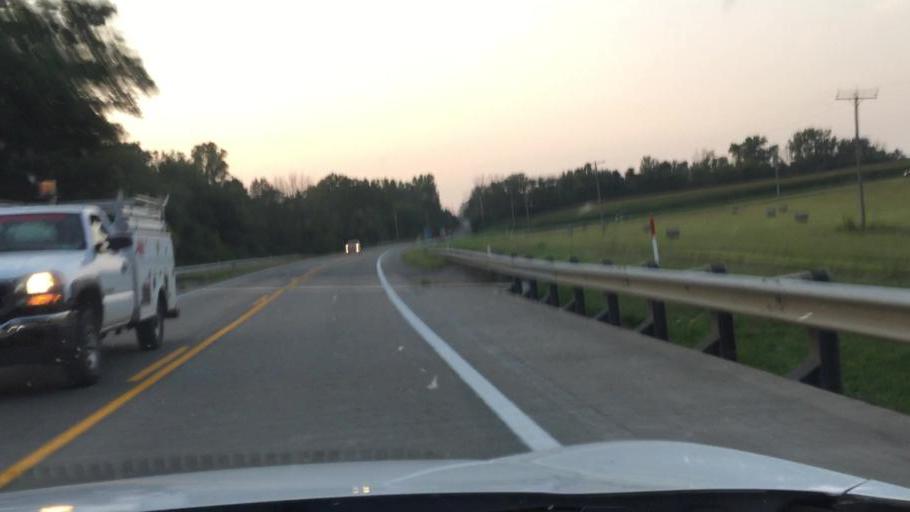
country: US
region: Ohio
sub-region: Madison County
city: Choctaw Lake
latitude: 39.9462
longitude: -83.5022
